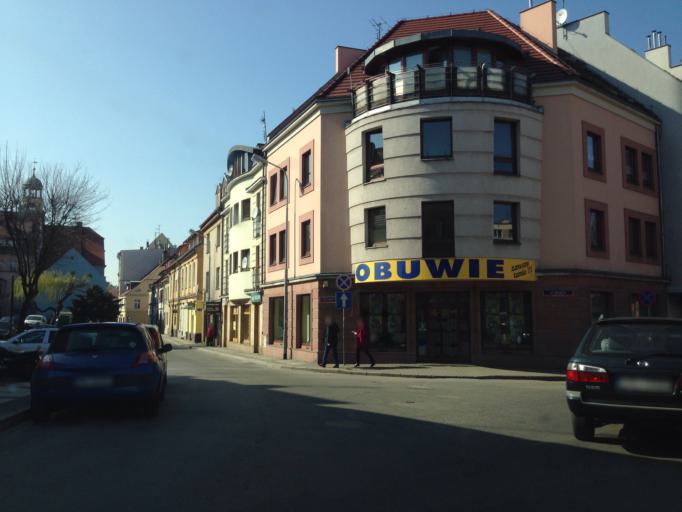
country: PL
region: Lower Silesian Voivodeship
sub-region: Powiat olesnicki
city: Olesnica
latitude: 51.2092
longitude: 17.3828
